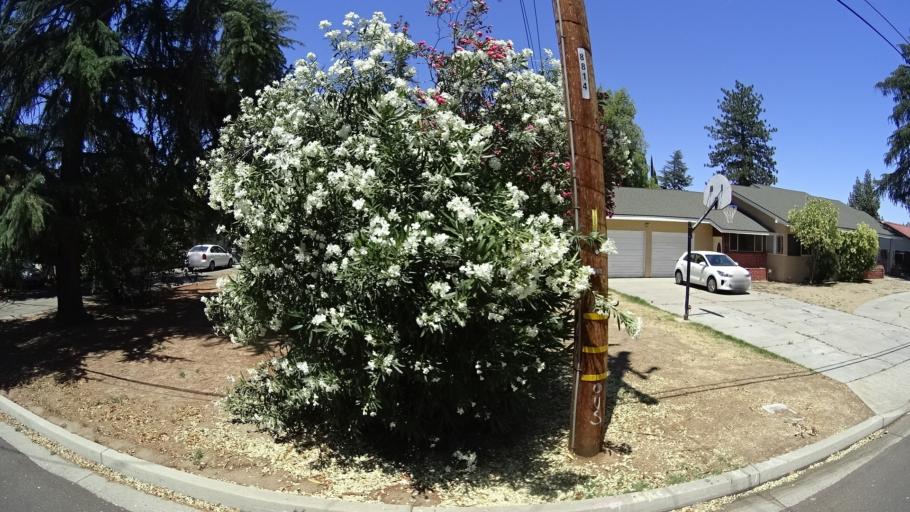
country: US
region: California
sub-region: Fresno County
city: Tarpey Village
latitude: 36.8032
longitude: -119.7465
